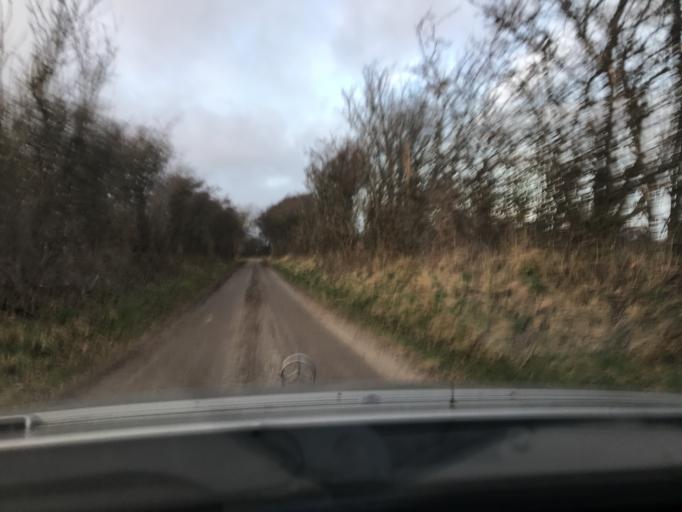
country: DK
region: South Denmark
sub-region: Sonderborg Kommune
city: Nordborg
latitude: 55.0618
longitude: 9.6699
